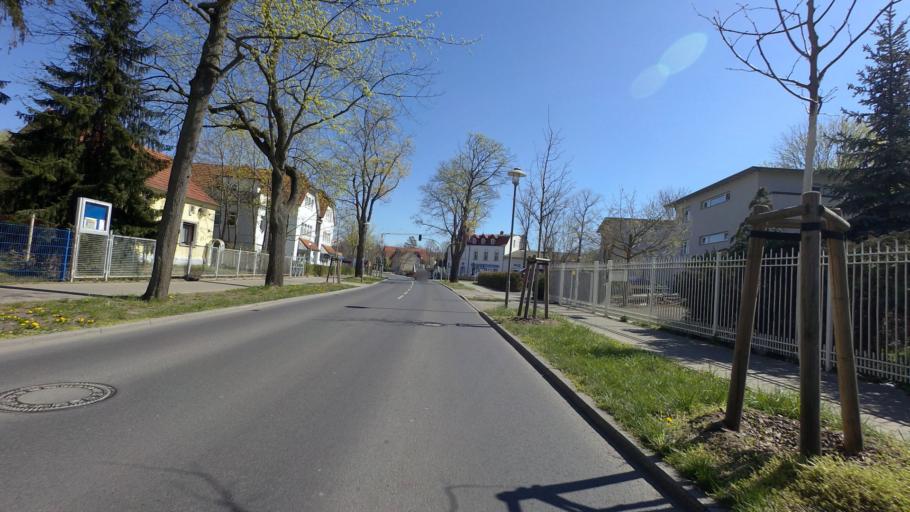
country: DE
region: Brandenburg
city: Zeuthen
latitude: 52.3394
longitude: 13.6076
